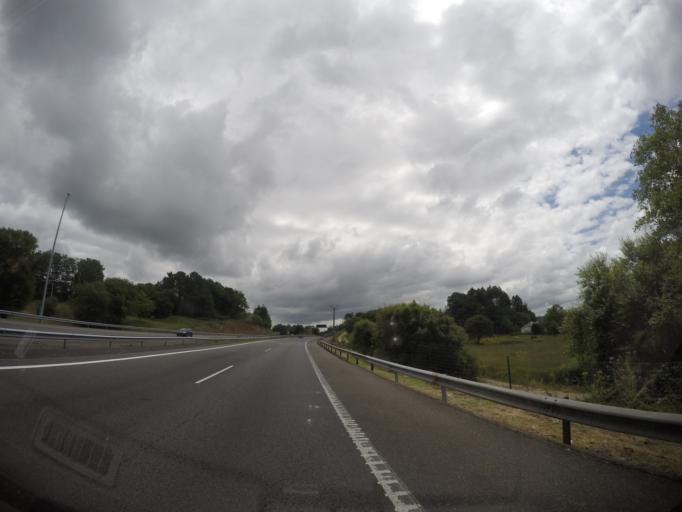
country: ES
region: Galicia
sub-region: Provincia da Coruna
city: Oleiros
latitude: 43.2927
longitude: -8.2977
